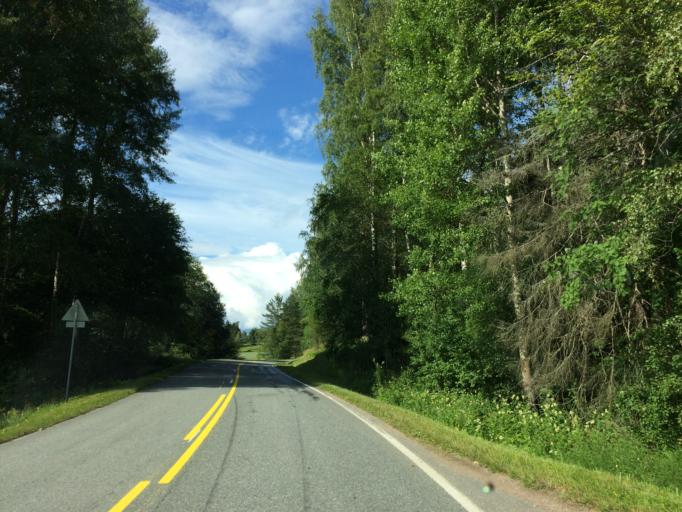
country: FI
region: Haeme
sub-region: Haemeenlinna
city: Janakkala
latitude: 60.8885
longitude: 24.5961
